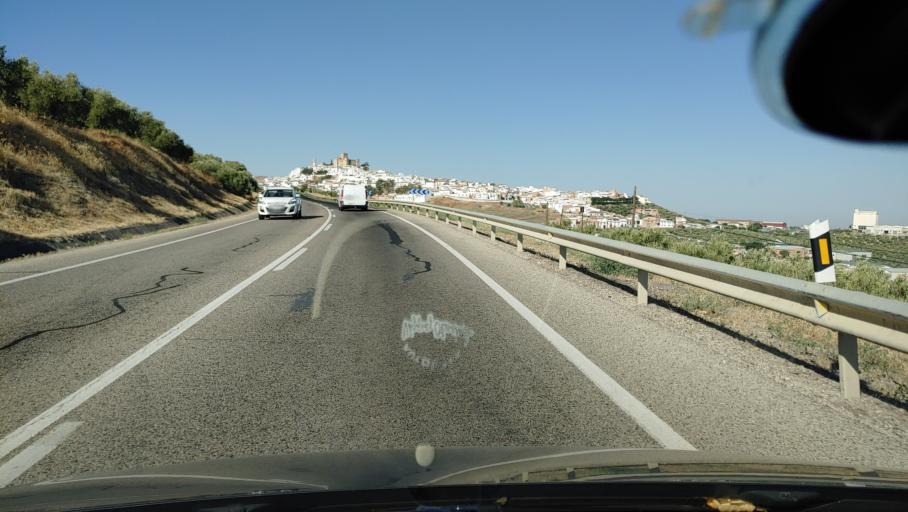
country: ES
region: Andalusia
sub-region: Province of Cordoba
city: Espejo
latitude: 37.6856
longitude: -4.5404
